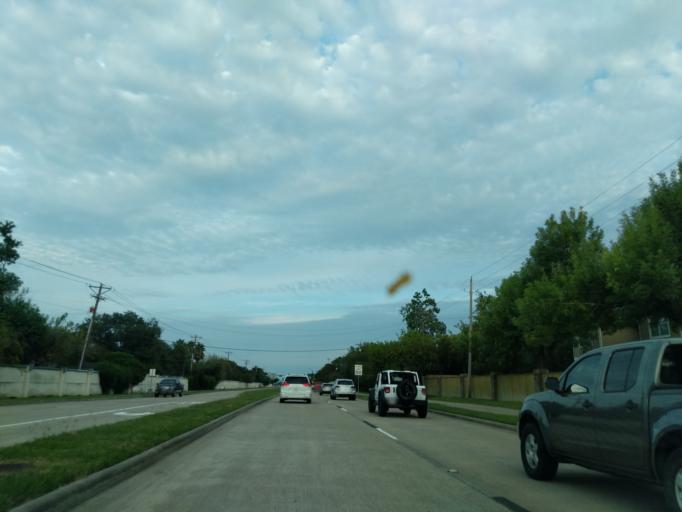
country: US
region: Texas
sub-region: Galveston County
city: Clear Lake Shores
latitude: 29.5250
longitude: -95.0602
